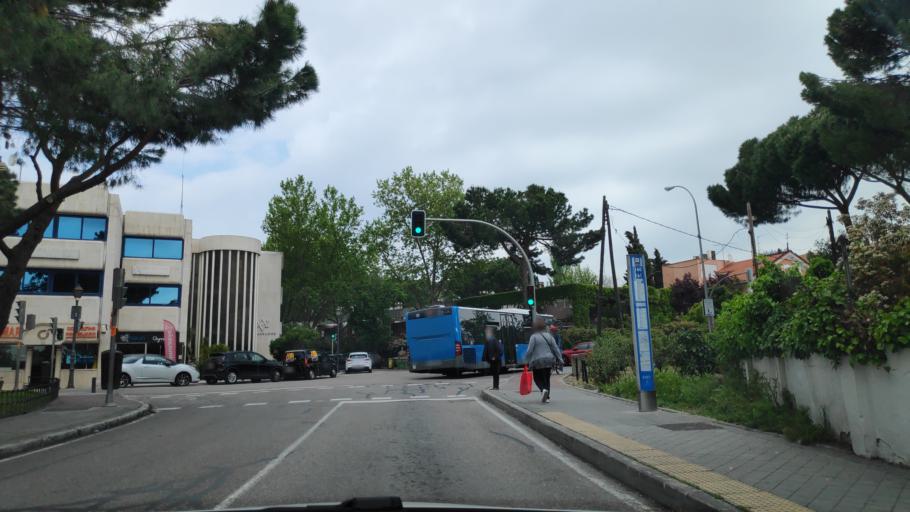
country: ES
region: Madrid
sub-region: Provincia de Madrid
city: Pozuelo de Alarcon
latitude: 40.4594
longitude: -3.7790
